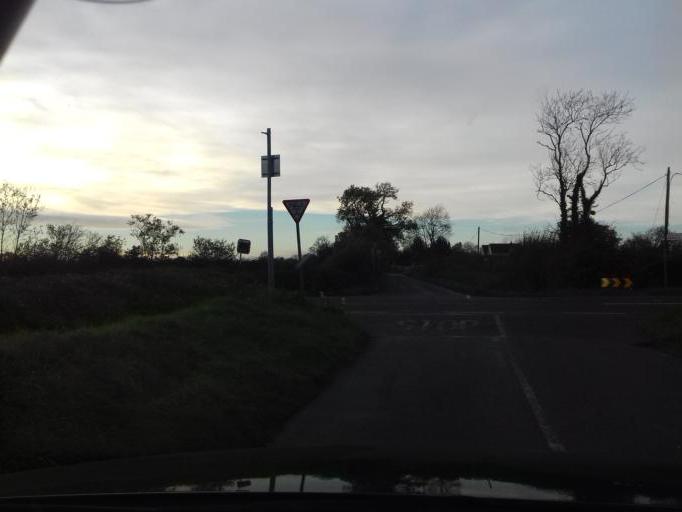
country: IE
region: Leinster
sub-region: An Mhi
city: Dunboyne
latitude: 53.3844
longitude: -6.4545
